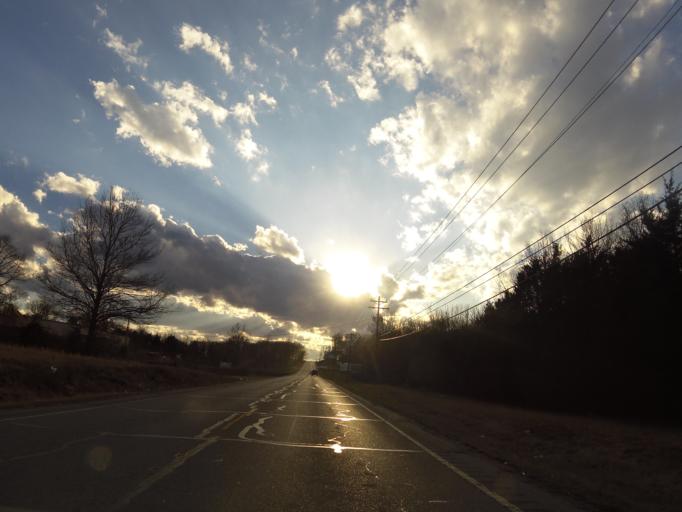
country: US
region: Tennessee
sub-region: Wilson County
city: Lebanon
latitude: 36.2142
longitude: -86.2618
